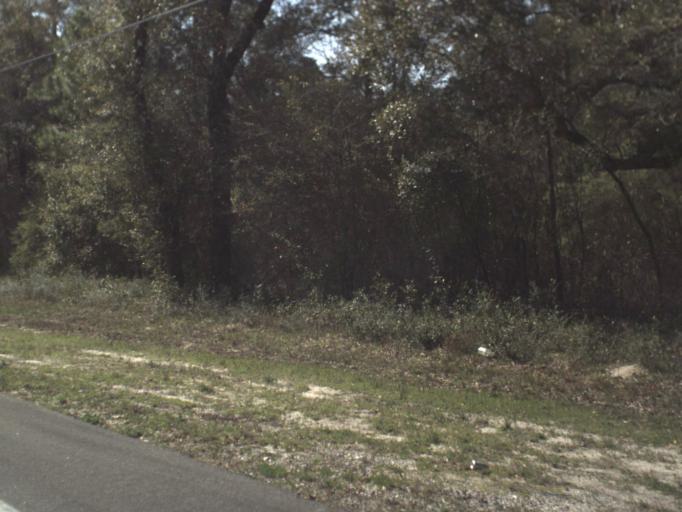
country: US
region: Florida
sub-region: Wakulla County
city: Crawfordville
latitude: 30.0775
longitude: -84.4034
